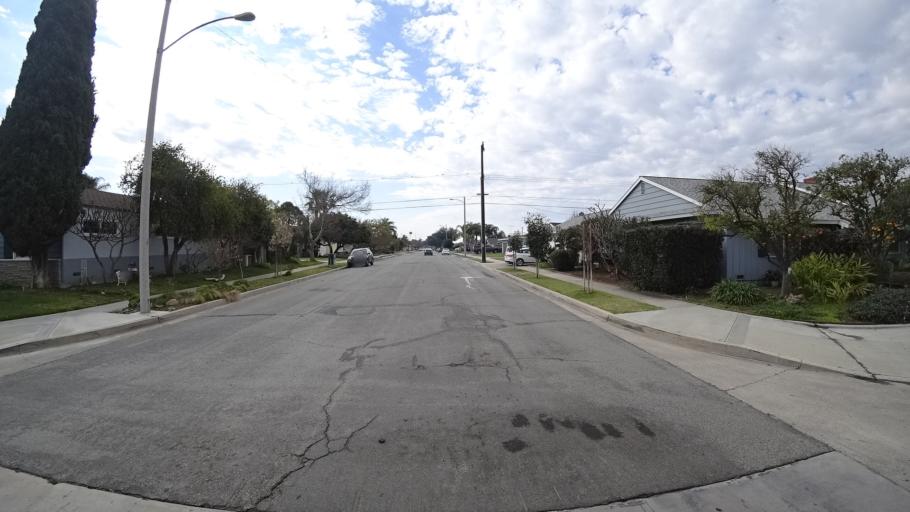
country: US
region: California
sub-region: Orange County
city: Placentia
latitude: 33.8512
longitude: -117.8855
